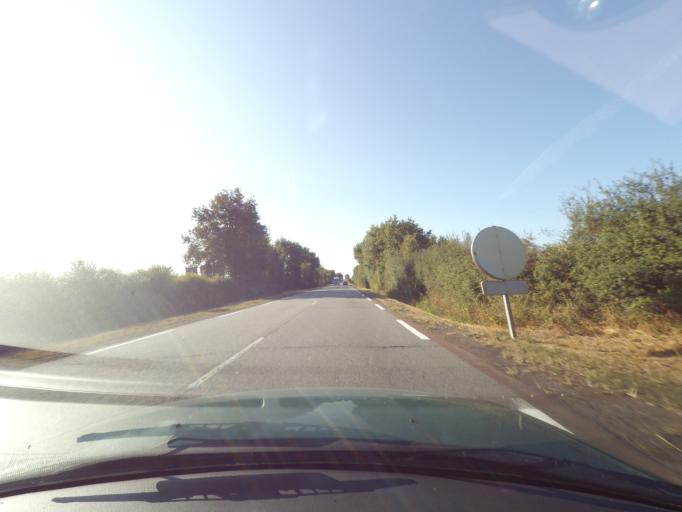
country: FR
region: Poitou-Charentes
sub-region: Departement des Deux-Sevres
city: Viennay
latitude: 46.6986
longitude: -0.2790
